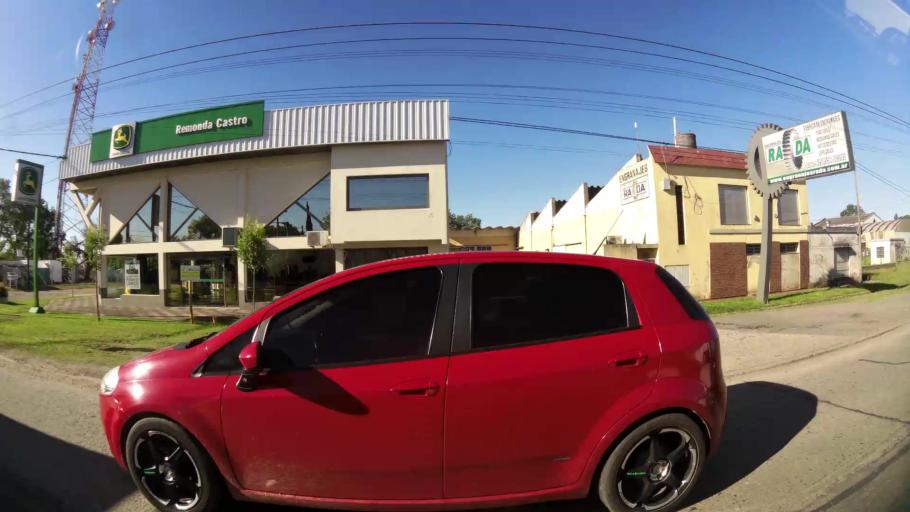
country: AR
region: Cordoba
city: San Francisco
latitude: -31.4179
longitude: -62.0752
